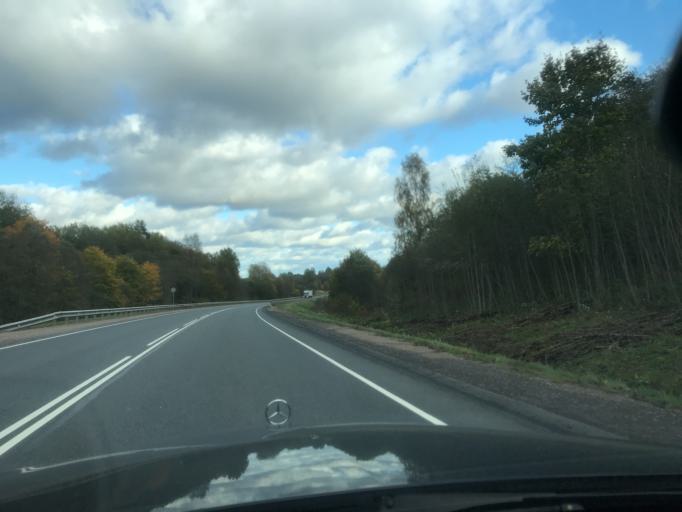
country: RU
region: Pskov
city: Novosokol'niki
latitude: 56.3486
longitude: 29.9173
